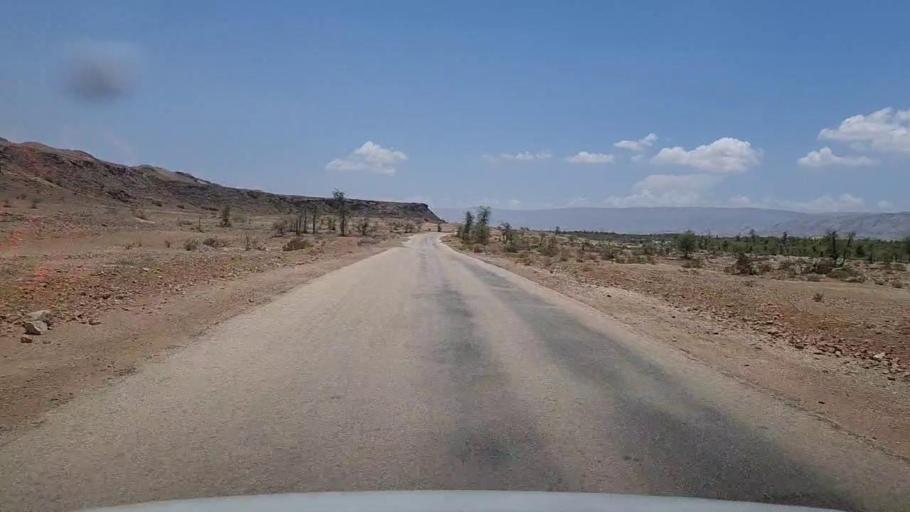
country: PK
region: Sindh
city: Bhan
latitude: 26.2974
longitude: 67.5343
